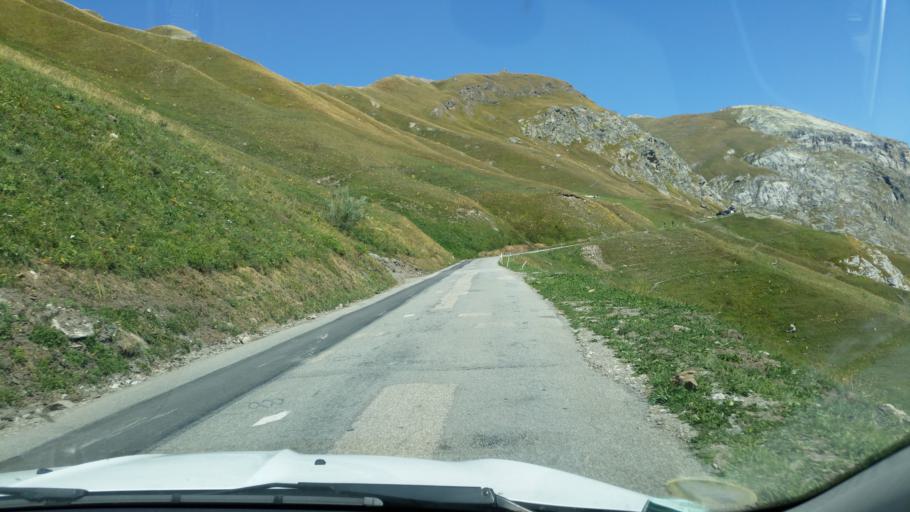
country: FR
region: Rhone-Alpes
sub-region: Departement de la Savoie
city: Val-d'Isere
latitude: 45.3740
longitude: 7.0356
